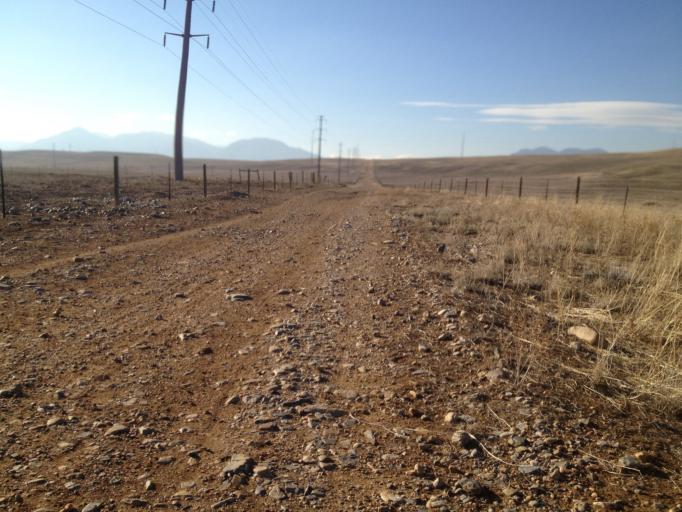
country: US
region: Colorado
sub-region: Boulder County
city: Superior
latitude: 39.9287
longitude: -105.1742
